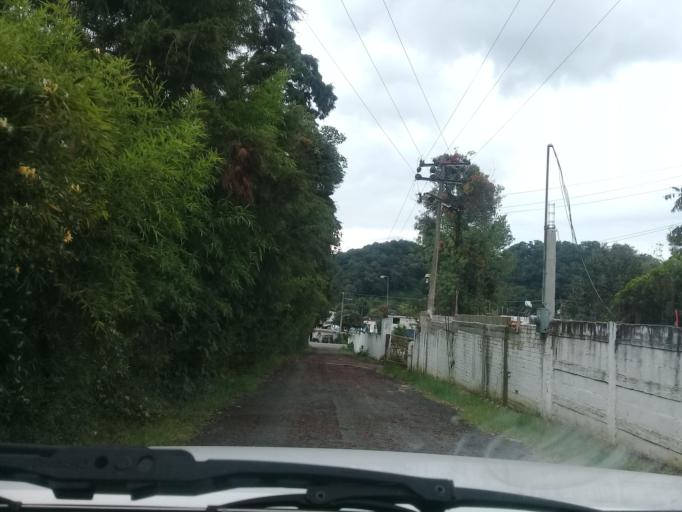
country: MX
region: Veracruz
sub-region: Rafael Lucio
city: Piletas
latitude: 19.5876
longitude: -96.9680
